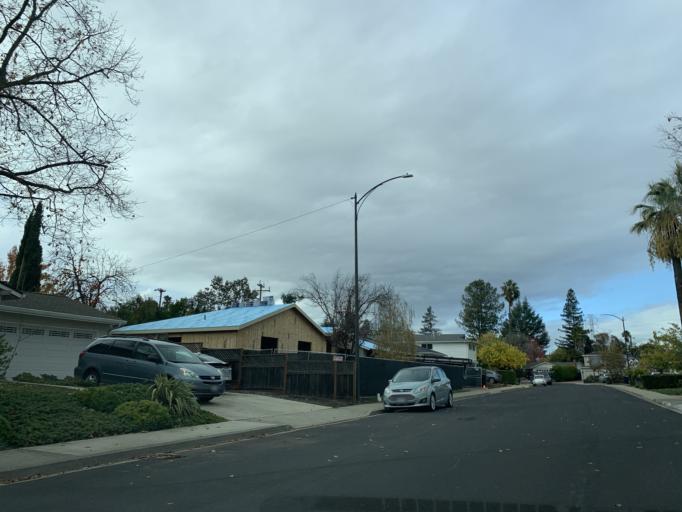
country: US
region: California
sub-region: Santa Clara County
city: Monte Sereno
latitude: 37.2619
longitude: -121.9793
